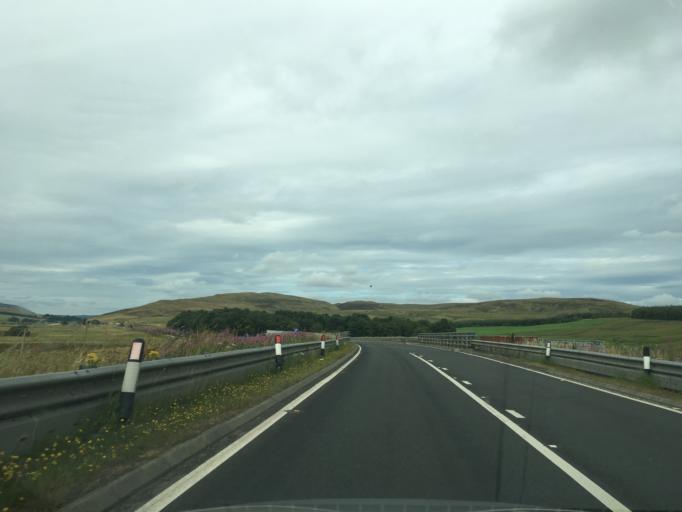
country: GB
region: Scotland
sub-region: South Lanarkshire
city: Douglas
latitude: 55.5237
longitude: -3.6759
